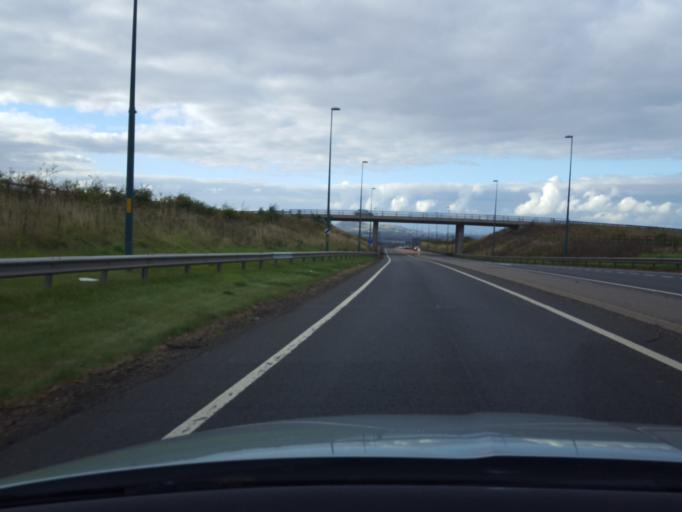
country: GB
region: Scotland
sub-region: Fife
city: Pathhead
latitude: 55.8933
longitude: -3.0011
